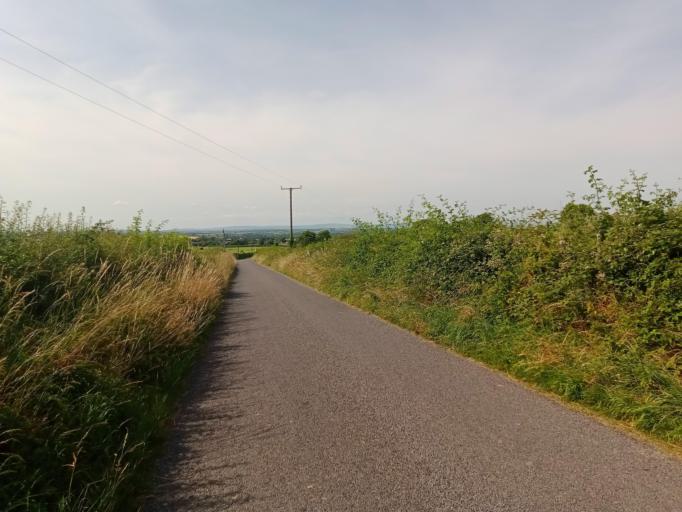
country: IE
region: Leinster
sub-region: Laois
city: Rathdowney
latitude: 52.8074
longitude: -7.4668
